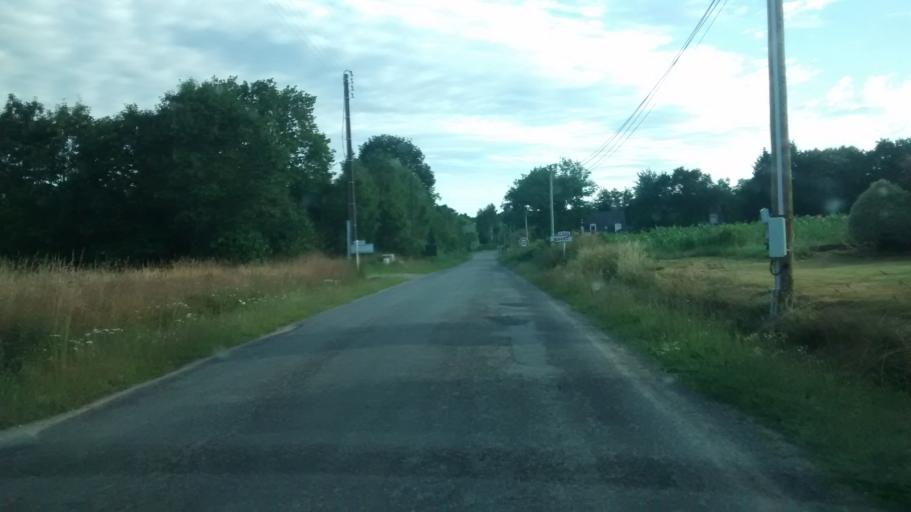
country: FR
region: Brittany
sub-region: Departement du Morbihan
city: Molac
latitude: 47.7337
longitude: -2.4358
